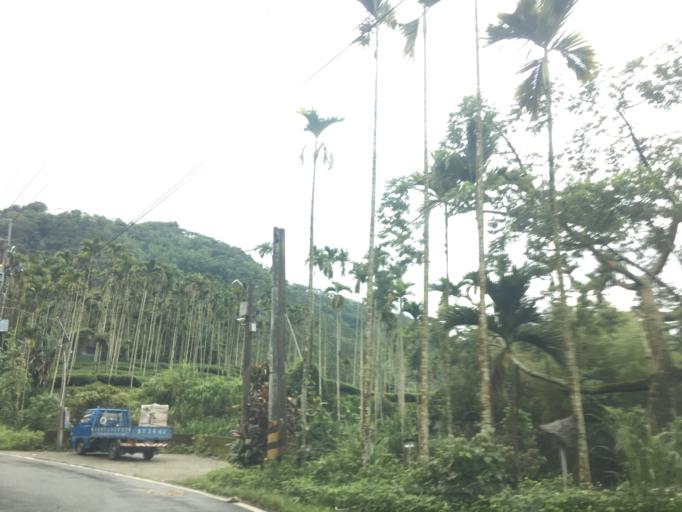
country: TW
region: Taiwan
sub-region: Yunlin
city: Douliu
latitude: 23.5619
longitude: 120.6473
